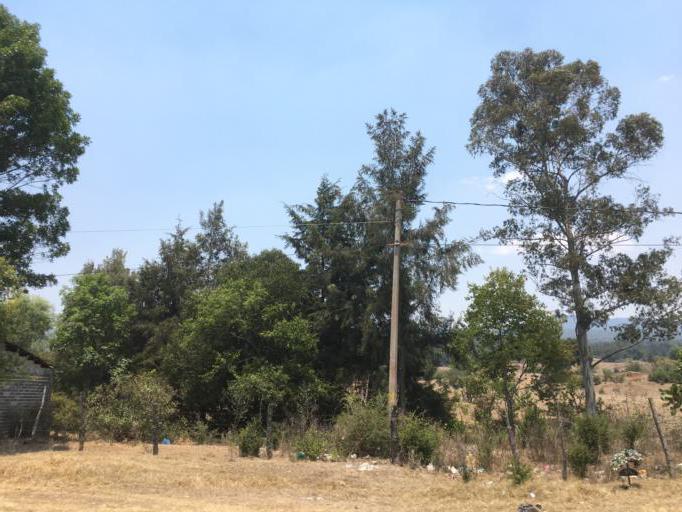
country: MX
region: Michoacan
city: Quiroga
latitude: 19.6482
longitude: -101.4922
